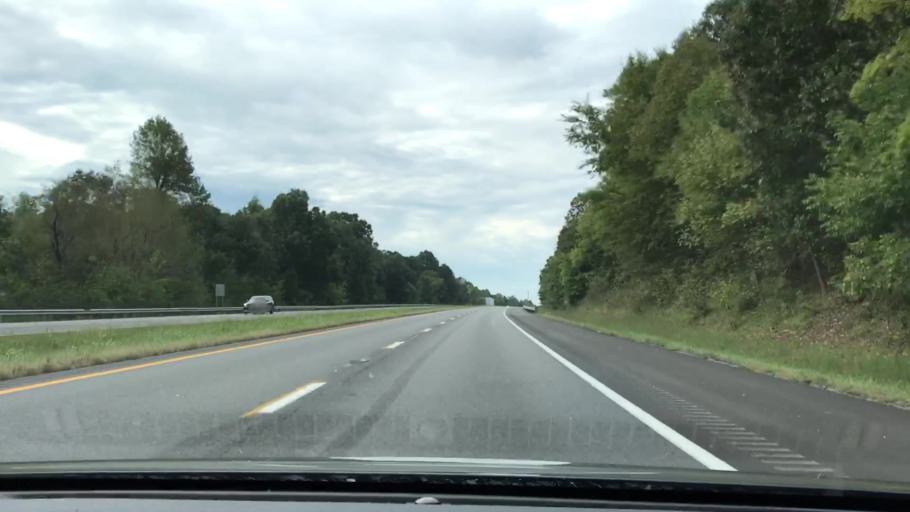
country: US
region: Kentucky
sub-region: Marshall County
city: Calvert City
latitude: 36.9778
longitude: -88.3458
